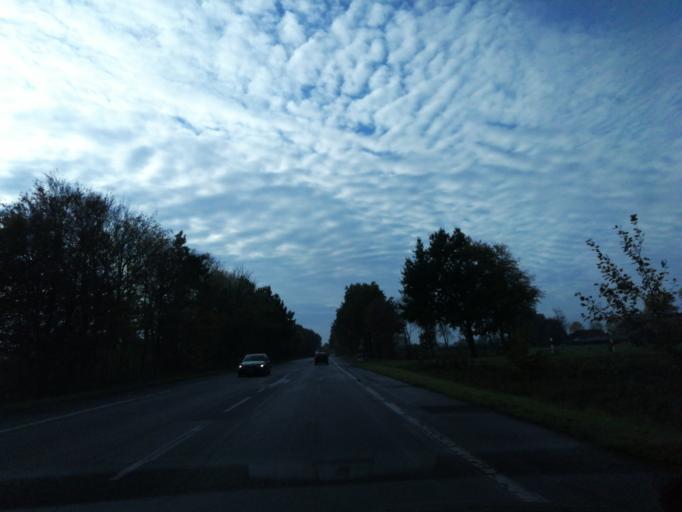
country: DE
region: Lower Saxony
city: Fedderwarden
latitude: 53.5763
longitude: 8.0567
